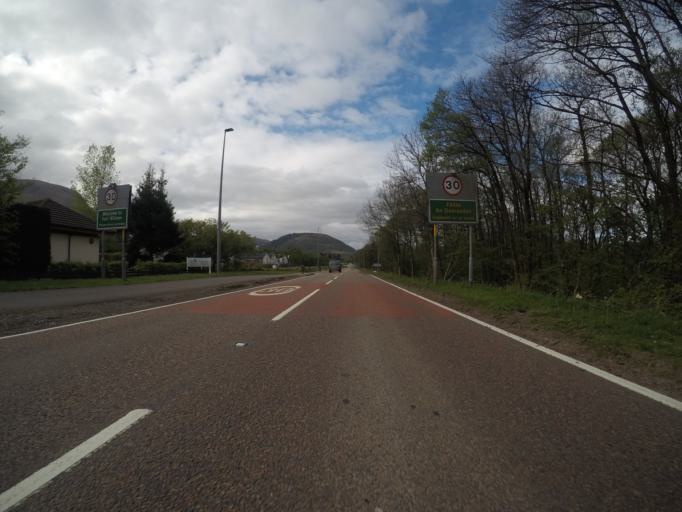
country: GB
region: Scotland
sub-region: Highland
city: Fort William
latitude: 56.8376
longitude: -5.0723
